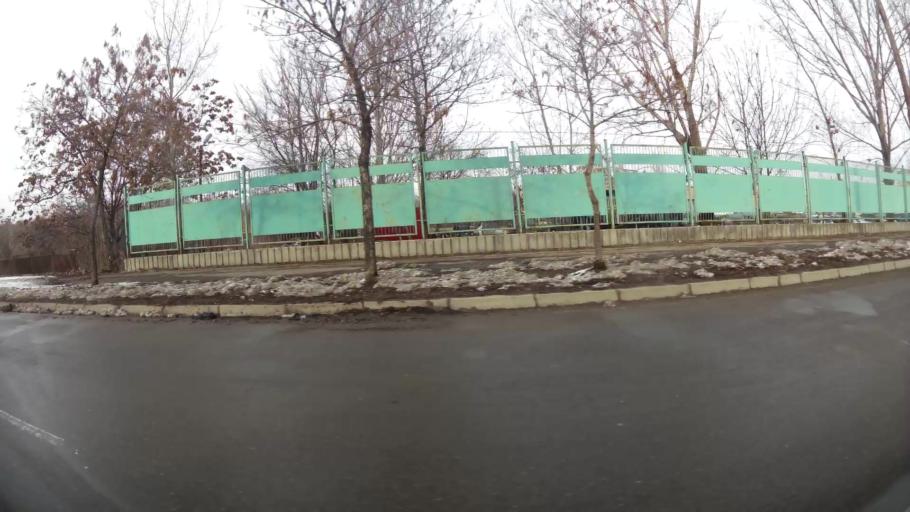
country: BG
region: Sofia-Capital
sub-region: Stolichna Obshtina
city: Sofia
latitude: 42.7115
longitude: 23.3611
